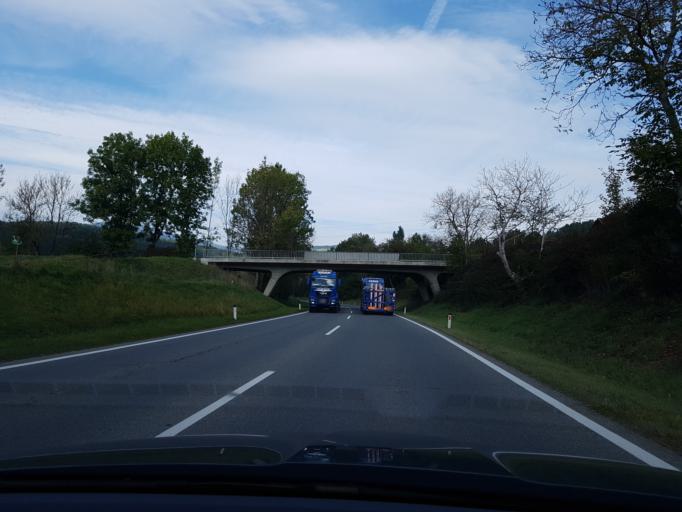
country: AT
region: Carinthia
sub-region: Politischer Bezirk Feldkirchen
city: Feldkirchen in Karnten
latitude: 46.7287
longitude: 14.1016
